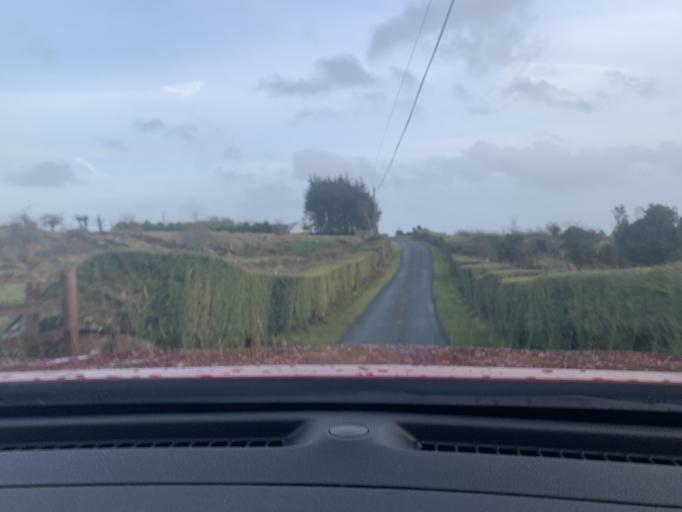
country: IE
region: Connaught
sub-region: Roscommon
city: Ballaghaderreen
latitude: 53.9495
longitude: -8.5141
